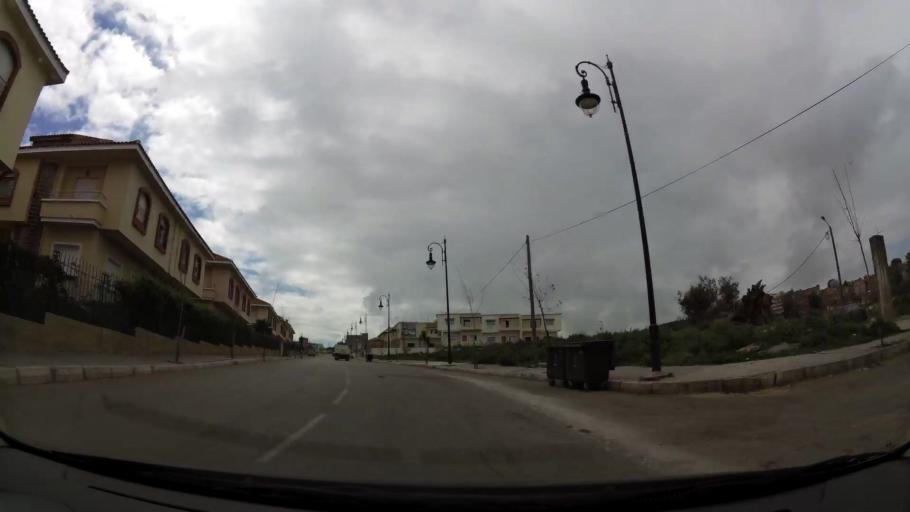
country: MA
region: Tanger-Tetouan
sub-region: Tanger-Assilah
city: Boukhalef
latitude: 35.7696
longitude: -5.8624
